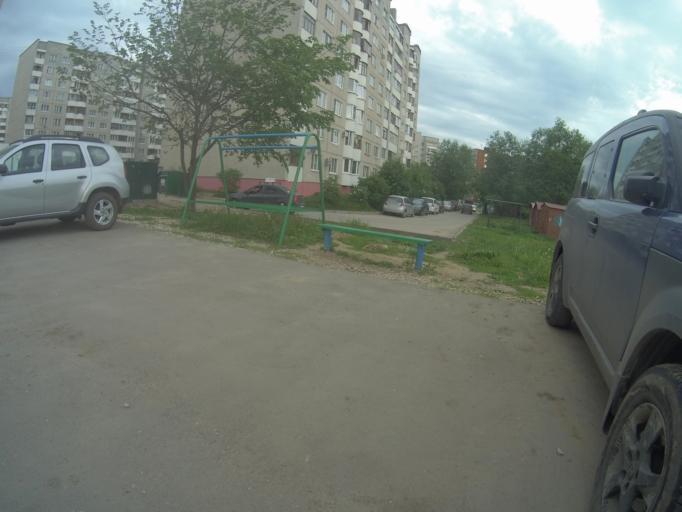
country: RU
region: Vladimir
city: Kommunar
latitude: 56.1627
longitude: 40.4600
